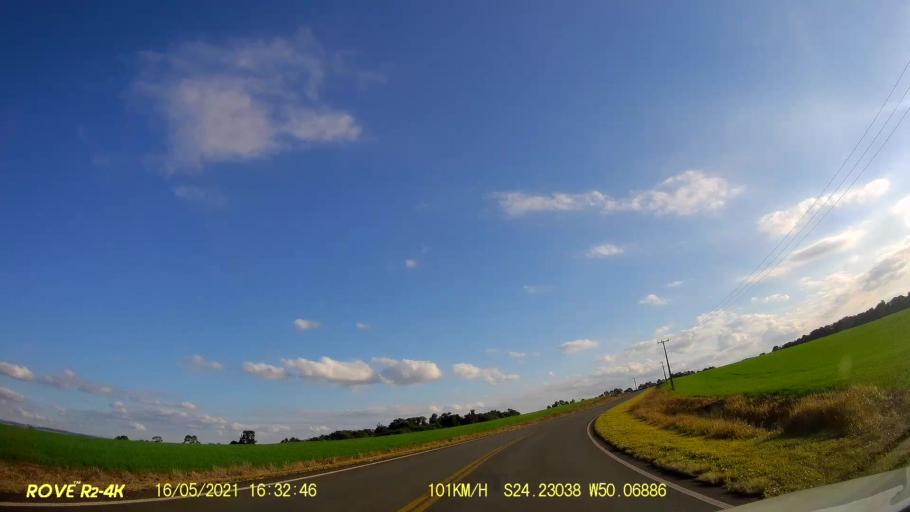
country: BR
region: Parana
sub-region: Pirai Do Sul
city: Pirai do Sul
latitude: -24.2308
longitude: -50.0691
